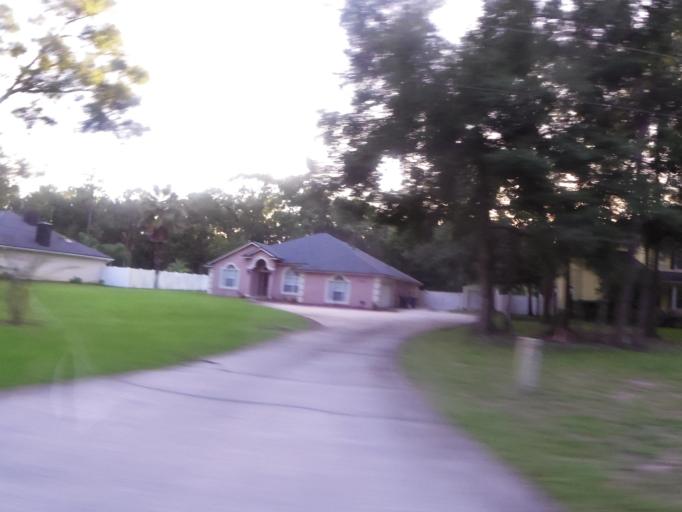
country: US
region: Florida
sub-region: Duval County
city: Atlantic Beach
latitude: 30.3652
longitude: -81.4843
